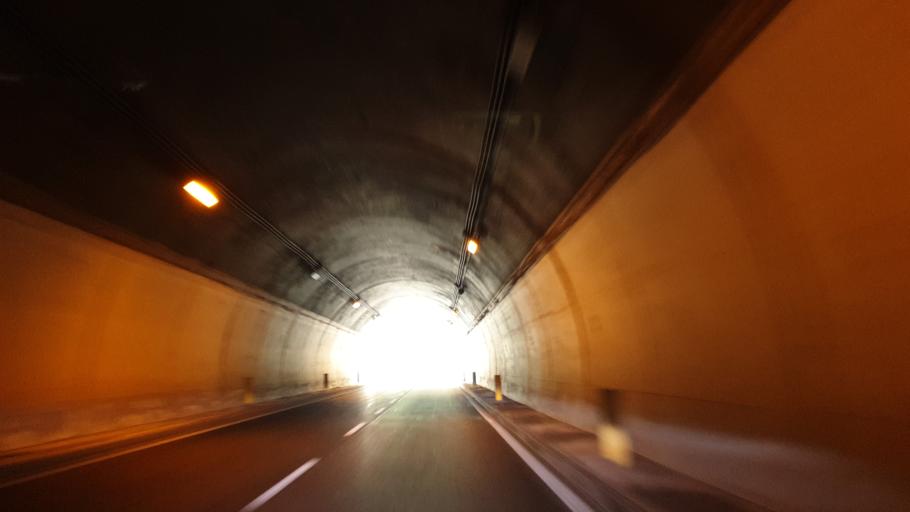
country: IT
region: Emilia-Romagna
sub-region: Forli-Cesena
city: Sarsina
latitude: 43.9165
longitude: 12.1435
